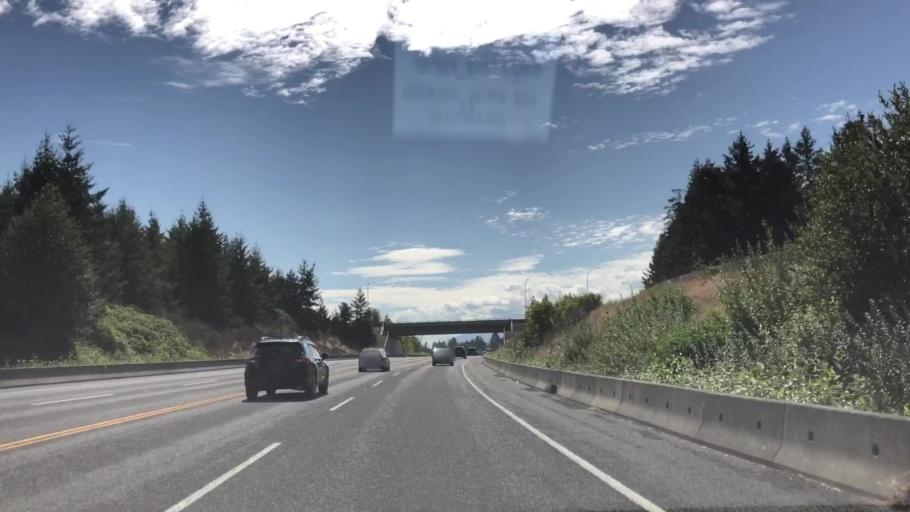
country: CA
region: British Columbia
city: Nanaimo
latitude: 49.1275
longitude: -123.8640
